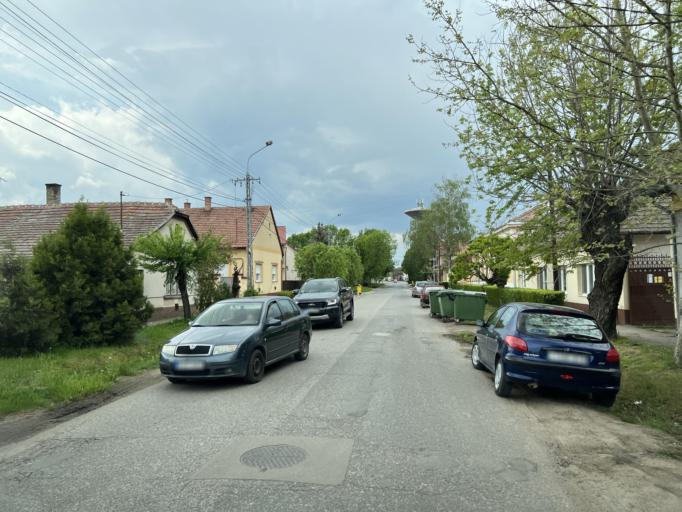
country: HU
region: Pest
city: Nagykoros
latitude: 47.0268
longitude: 19.7854
